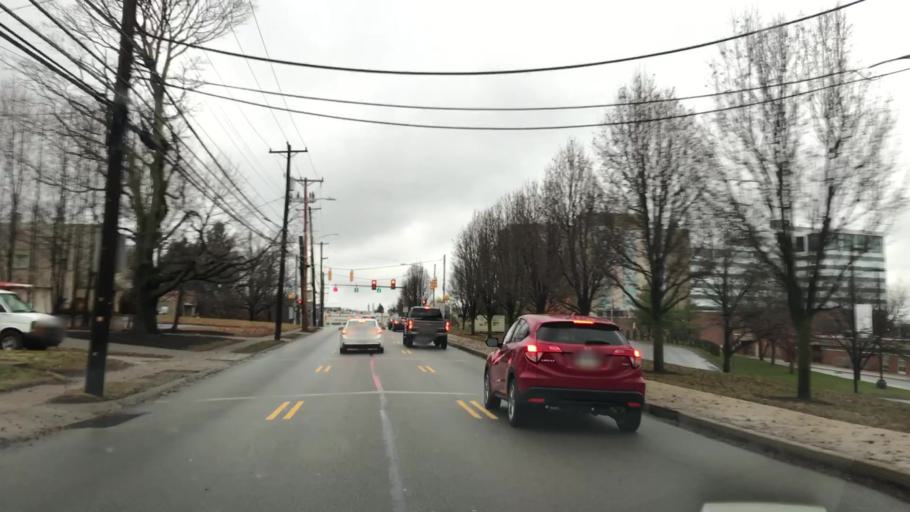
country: US
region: Pennsylvania
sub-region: Allegheny County
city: Green Tree
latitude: 40.4235
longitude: -80.0443
